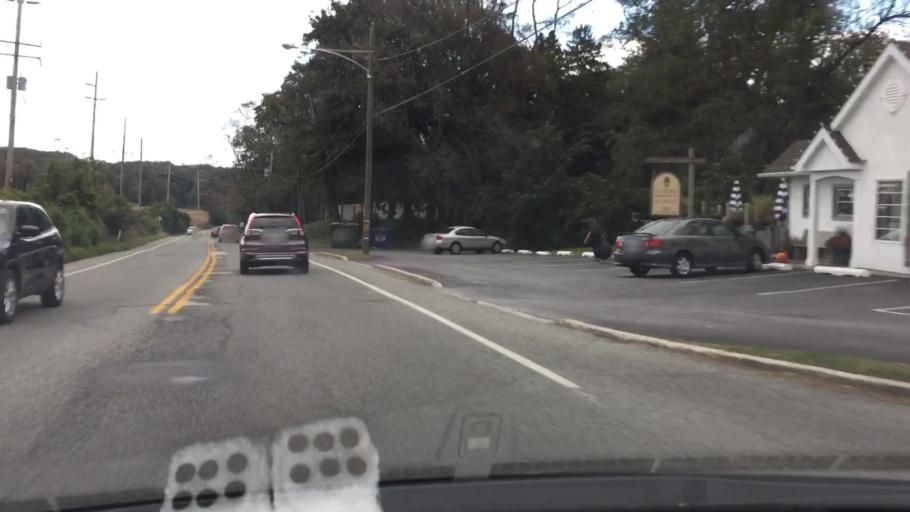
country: US
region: Pennsylvania
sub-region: Delaware County
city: Lima
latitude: 39.9391
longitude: -75.4601
